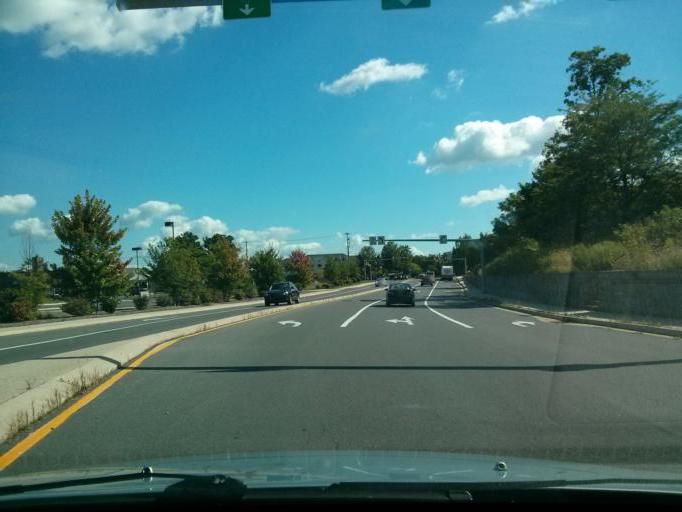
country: US
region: Pennsylvania
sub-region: Centre County
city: Park Forest Village
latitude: 40.8153
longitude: -77.9013
